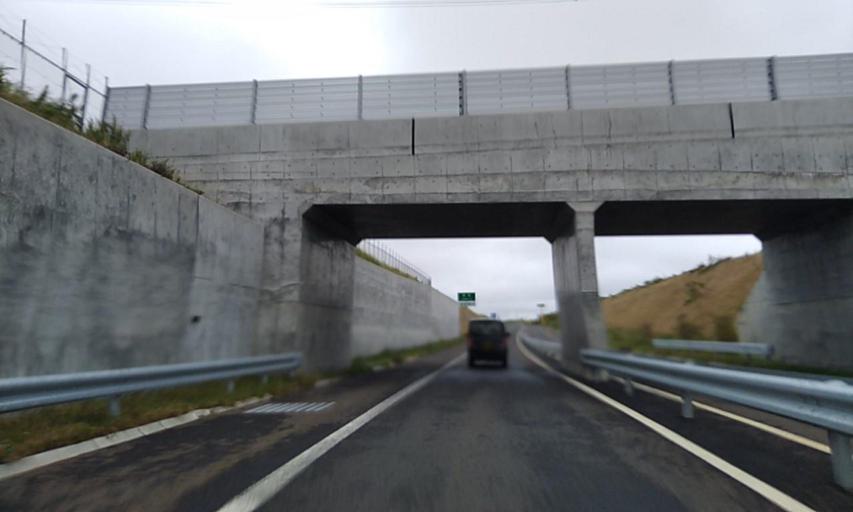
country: JP
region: Hokkaido
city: Nemuro
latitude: 43.3122
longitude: 145.5456
